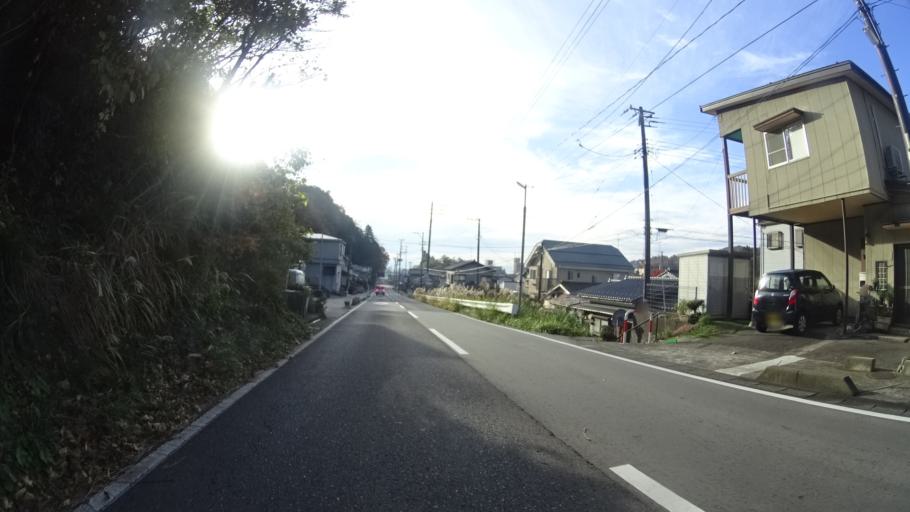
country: JP
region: Niigata
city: Yoshida-kasugacho
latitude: 37.7030
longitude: 138.8314
